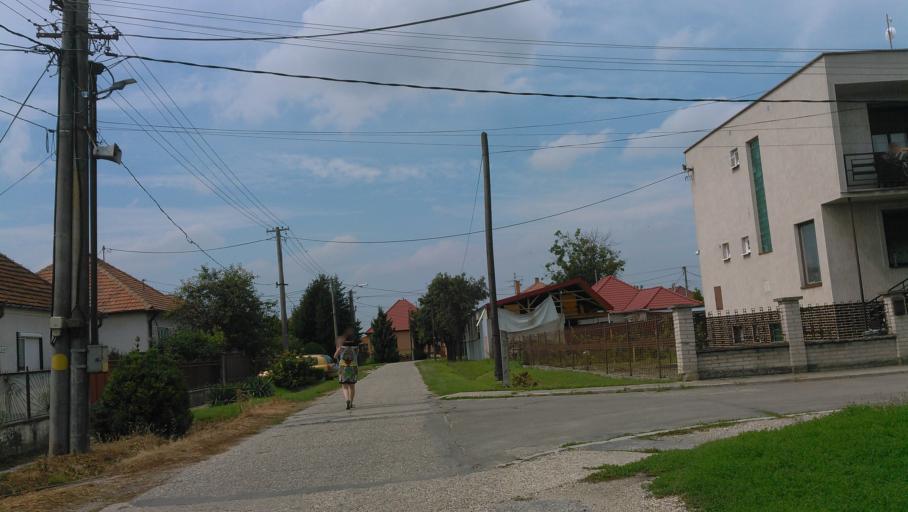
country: SK
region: Nitriansky
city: Kolarovo
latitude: 47.9027
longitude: 18.0038
